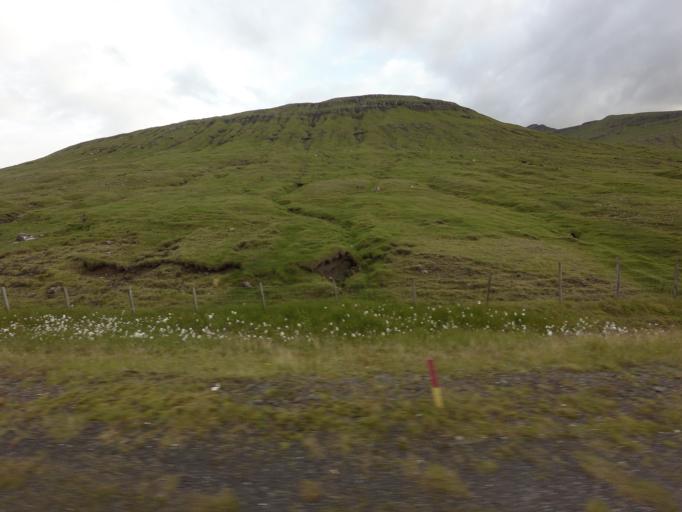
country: FO
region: Streymoy
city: Kollafjordhur
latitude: 62.1810
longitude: -6.9967
